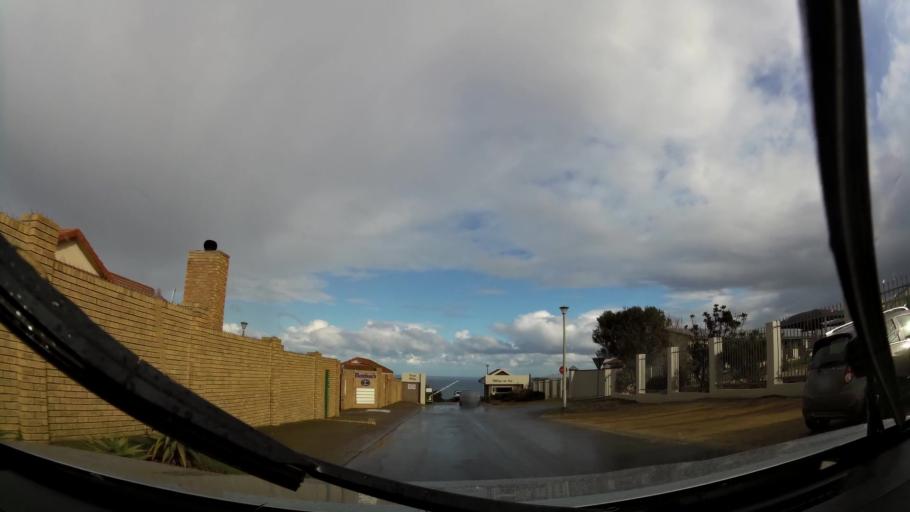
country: ZA
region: Western Cape
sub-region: Eden District Municipality
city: Mossel Bay
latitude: -34.1942
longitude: 22.1139
